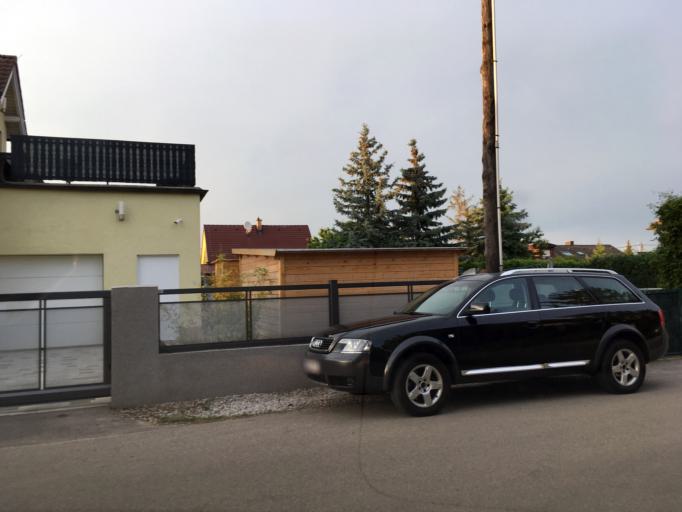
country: AT
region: Lower Austria
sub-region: Politischer Bezirk Wien-Umgebung
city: Gerasdorf bei Wien
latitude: 48.3160
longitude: 16.4964
